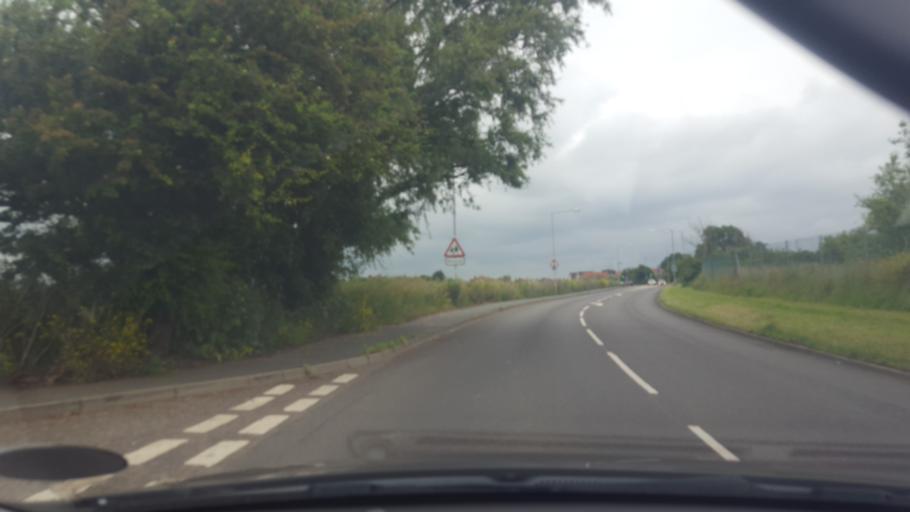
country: GB
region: England
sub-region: Essex
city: Saint Osyth
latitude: 51.7914
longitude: 1.1180
